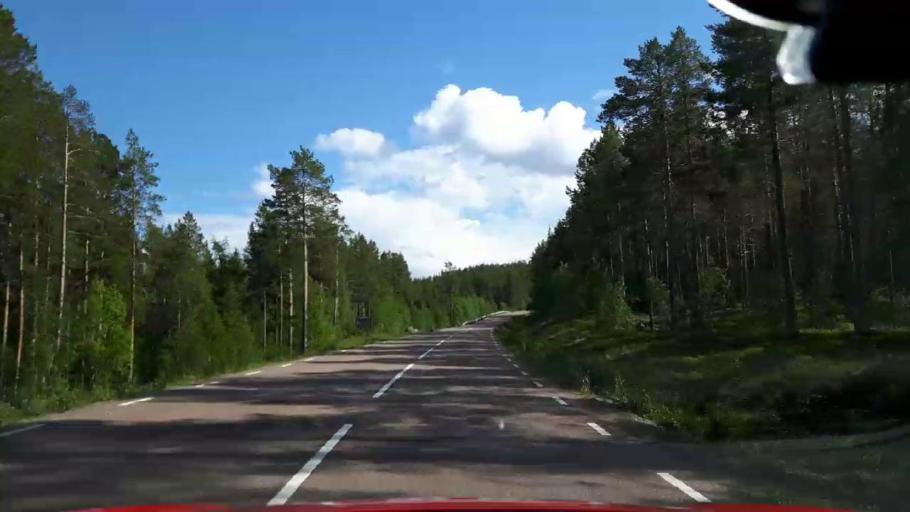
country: SE
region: Jaemtland
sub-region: Krokoms Kommun
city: Valla
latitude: 64.0072
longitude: 14.2380
